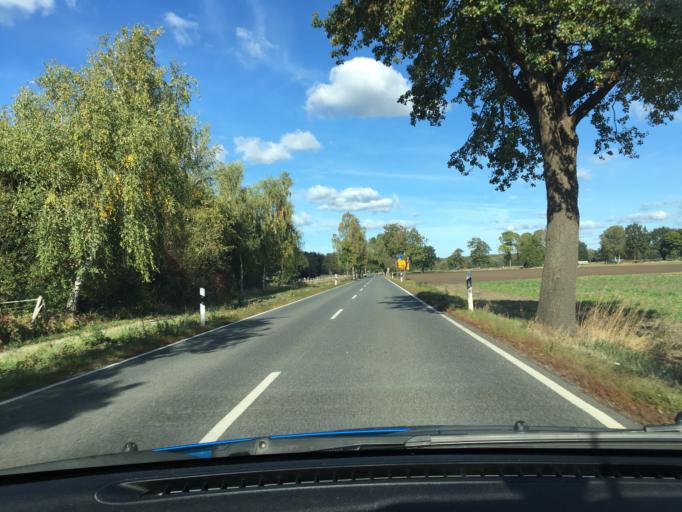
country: DE
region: Lower Saxony
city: Isernhagen Farster Bauerschaft
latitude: 52.5138
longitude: 9.8596
